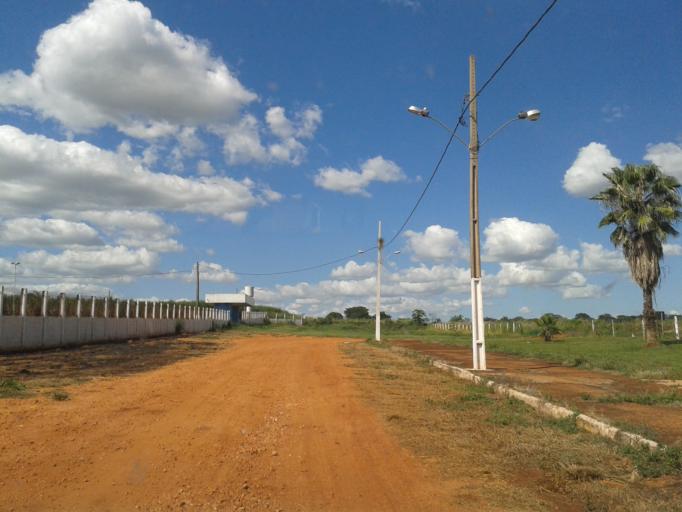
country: BR
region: Minas Gerais
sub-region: Santa Vitoria
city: Santa Vitoria
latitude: -18.6955
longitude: -49.9338
